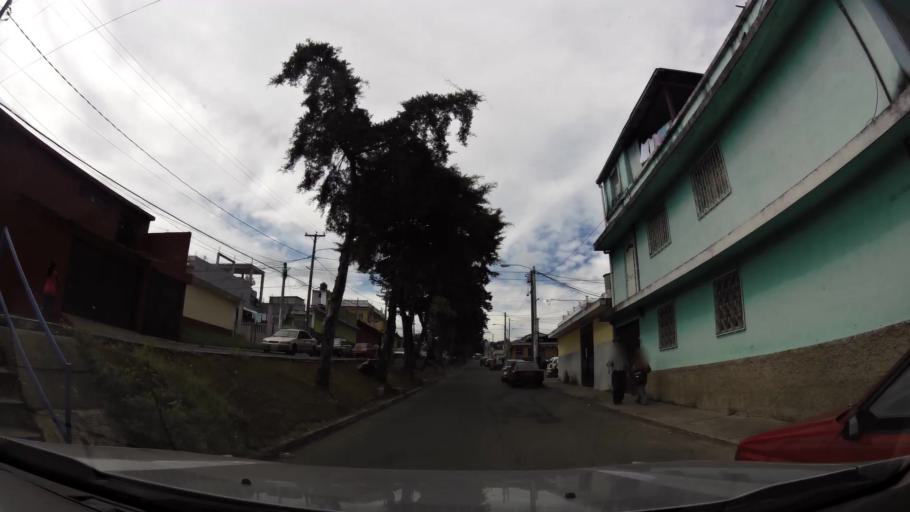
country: GT
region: Guatemala
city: Mixco
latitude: 14.6735
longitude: -90.5640
